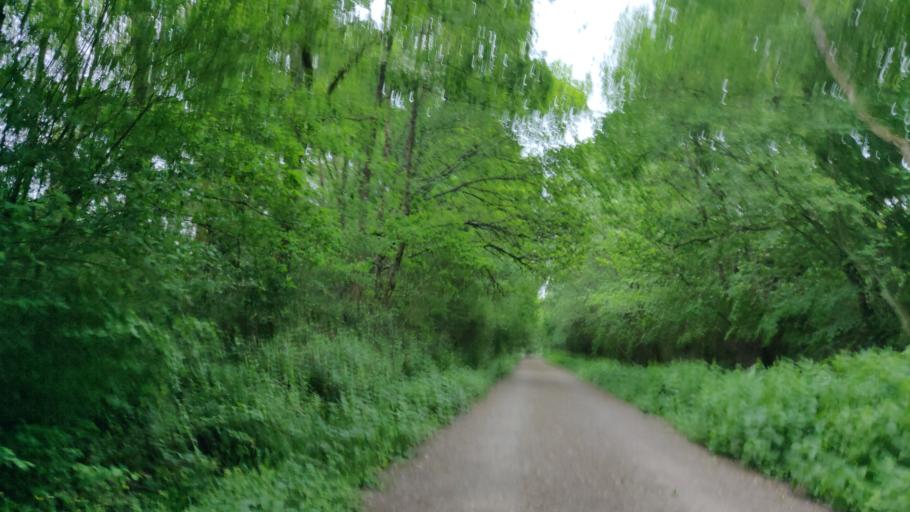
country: GB
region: England
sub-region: West Sussex
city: Southwater
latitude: 51.0068
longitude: -0.3273
